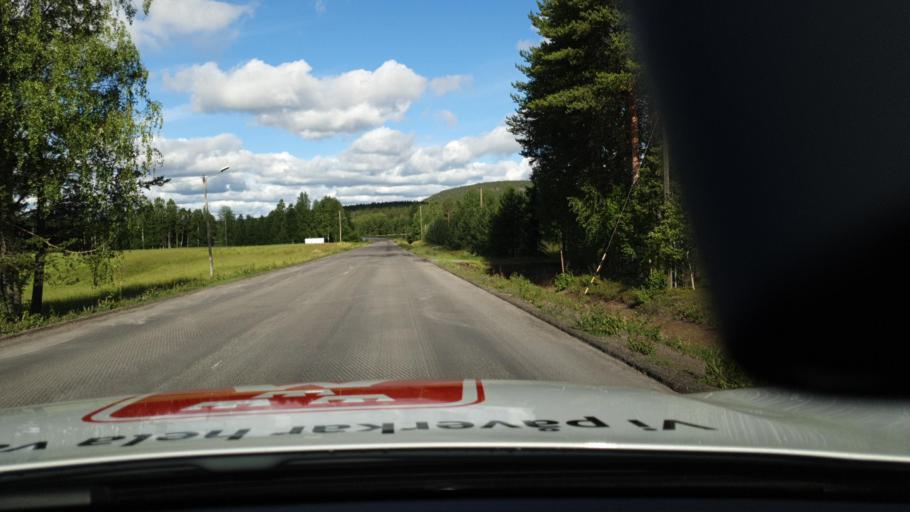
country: SE
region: Norrbotten
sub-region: Bodens Kommun
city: Boden
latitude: 65.8567
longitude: 21.4720
